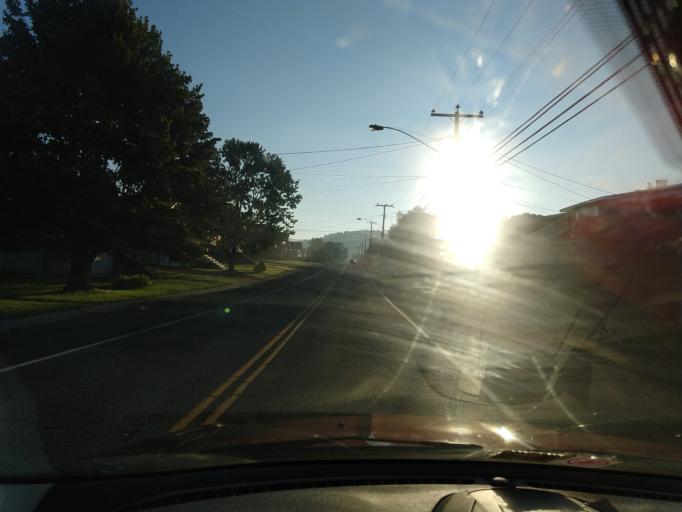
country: US
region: Virginia
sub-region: City of Covington
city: Fairlawn
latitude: 37.7643
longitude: -79.9993
